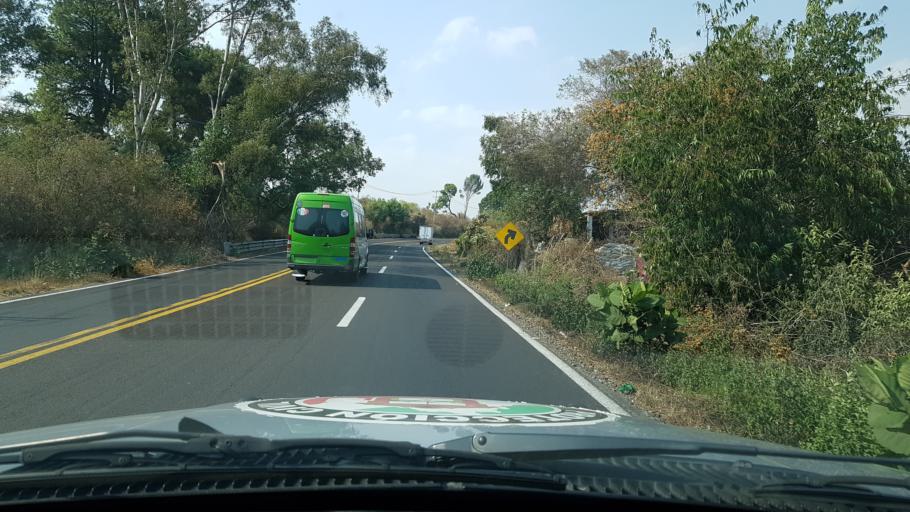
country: MX
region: Mexico
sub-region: Ozumba
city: San Jose Tlacotitlan
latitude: 18.9982
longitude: -98.8228
